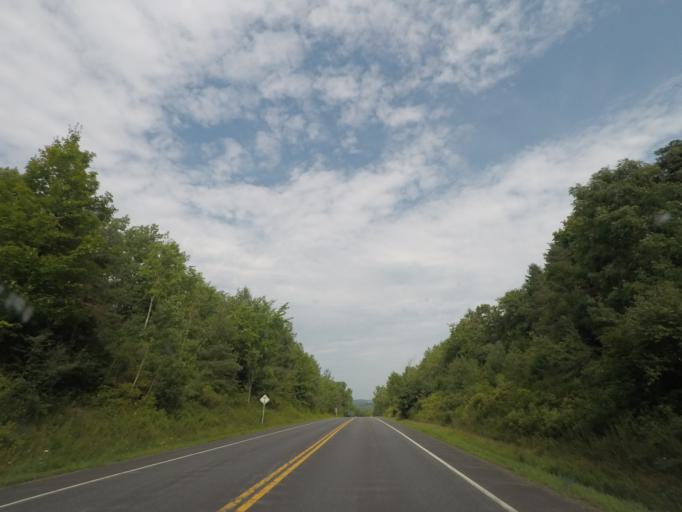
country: US
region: New York
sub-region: Rensselaer County
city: Poestenkill
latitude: 42.7295
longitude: -73.5578
